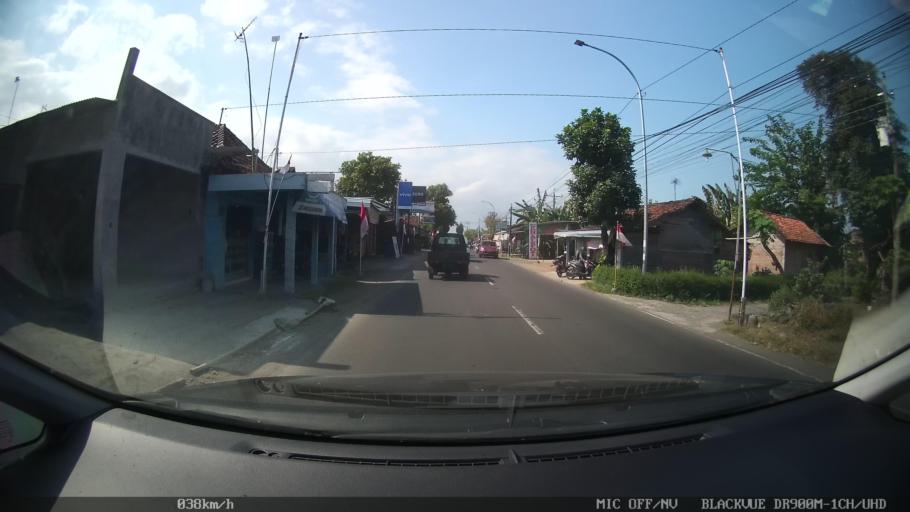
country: ID
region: Daerah Istimewa Yogyakarta
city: Sewon
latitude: -7.8783
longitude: 110.3907
